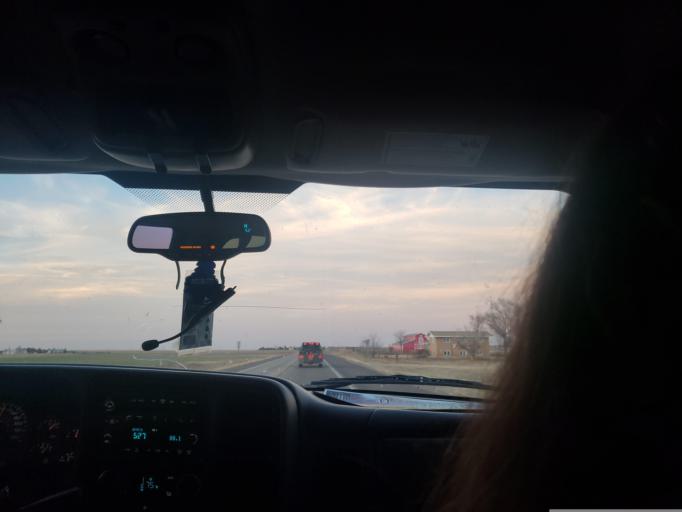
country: US
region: Kansas
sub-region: Seward County
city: Liberal
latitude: 37.0765
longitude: -100.9225
